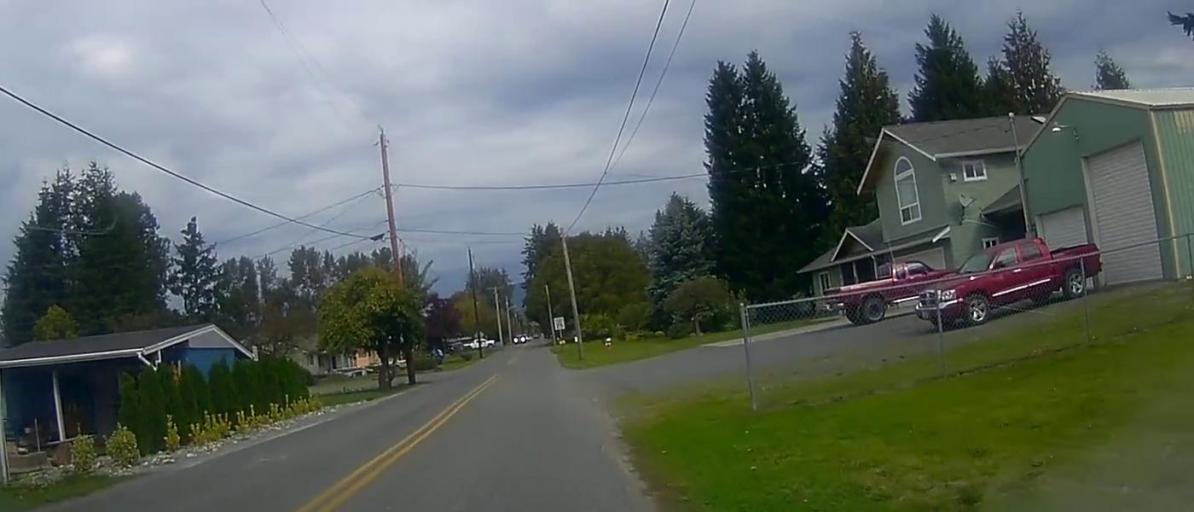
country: US
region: Washington
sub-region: Skagit County
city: Sedro-Woolley
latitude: 48.4970
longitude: -122.2583
